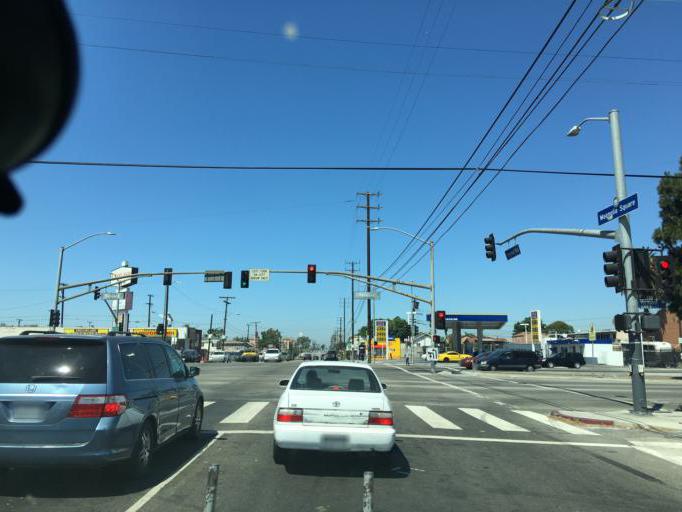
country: US
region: California
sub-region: Los Angeles County
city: West Athens
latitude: 33.9310
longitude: -118.2913
